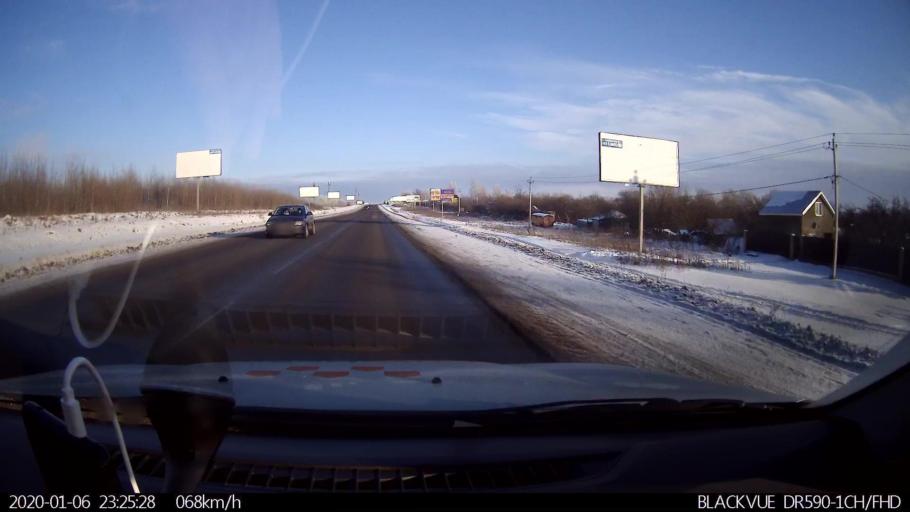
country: RU
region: Nizjnij Novgorod
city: Burevestnik
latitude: 56.2015
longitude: 43.8572
